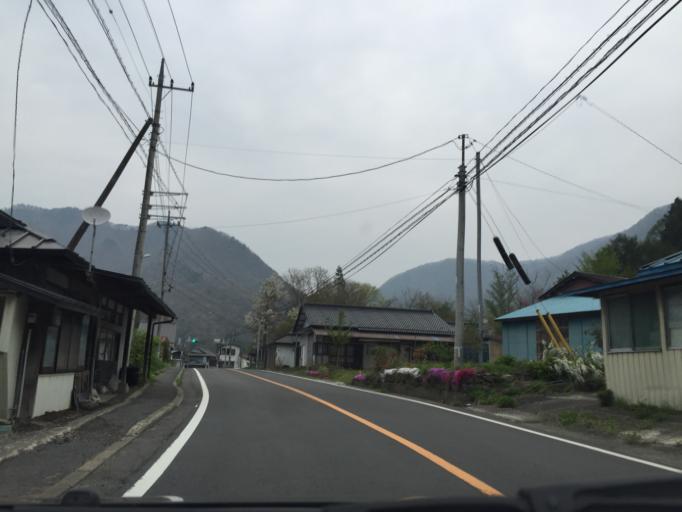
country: JP
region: Tochigi
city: Nikko
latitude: 36.9841
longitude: 139.6939
